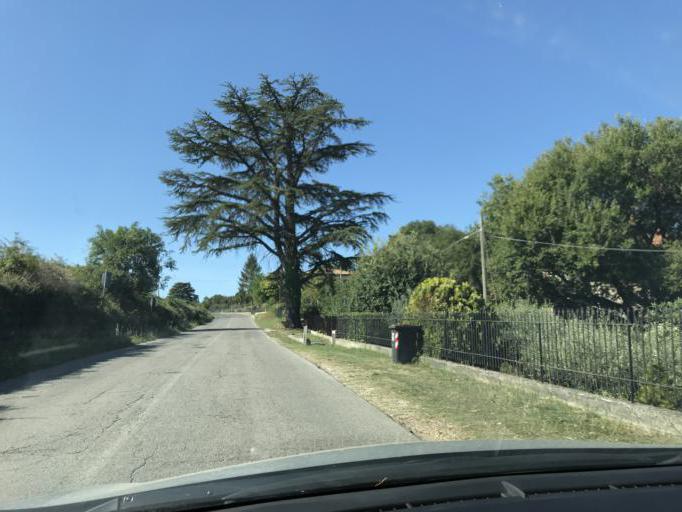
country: IT
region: Umbria
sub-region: Provincia di Terni
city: Fornole
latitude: 42.5619
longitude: 12.4438
